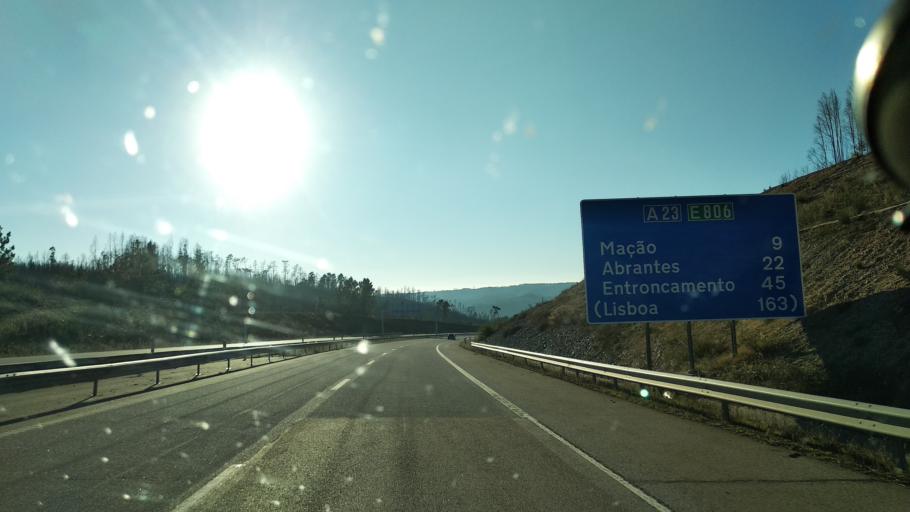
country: PT
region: Santarem
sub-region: Macao
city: Macao
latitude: 39.5270
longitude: -7.9598
